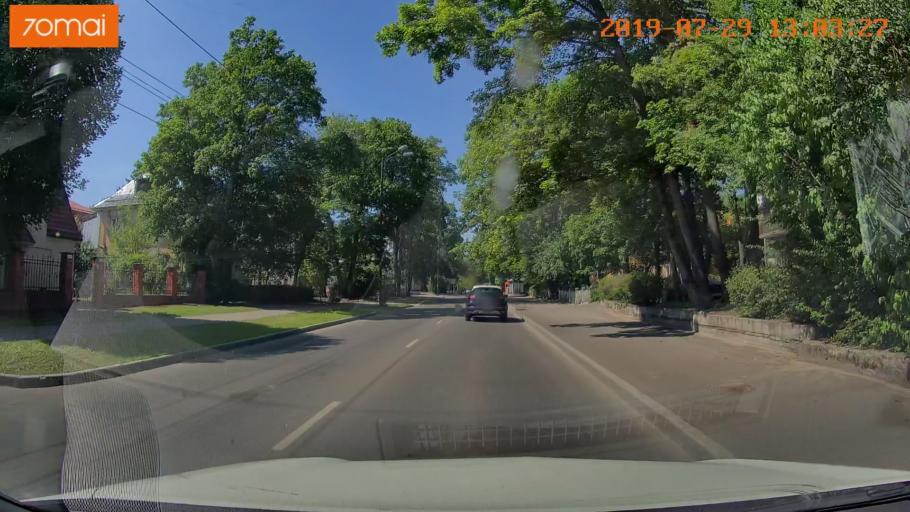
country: RU
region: Kaliningrad
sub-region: Gorod Kaliningrad
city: Kaliningrad
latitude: 54.7151
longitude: 20.4676
